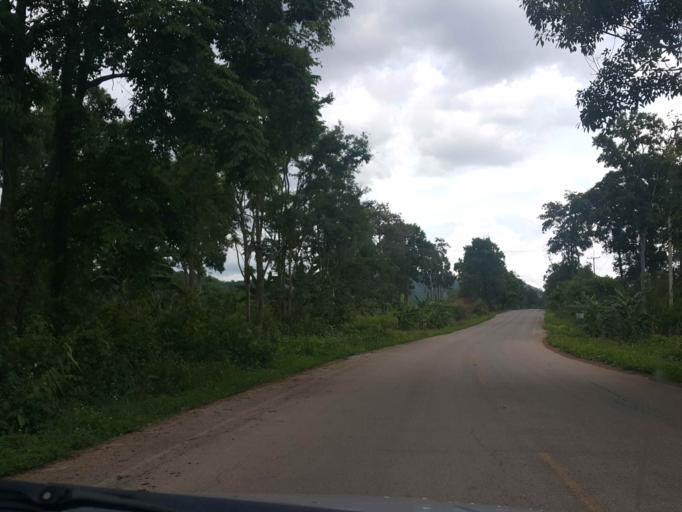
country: TH
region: Lampang
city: Ngao
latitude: 18.9369
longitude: 100.0811
